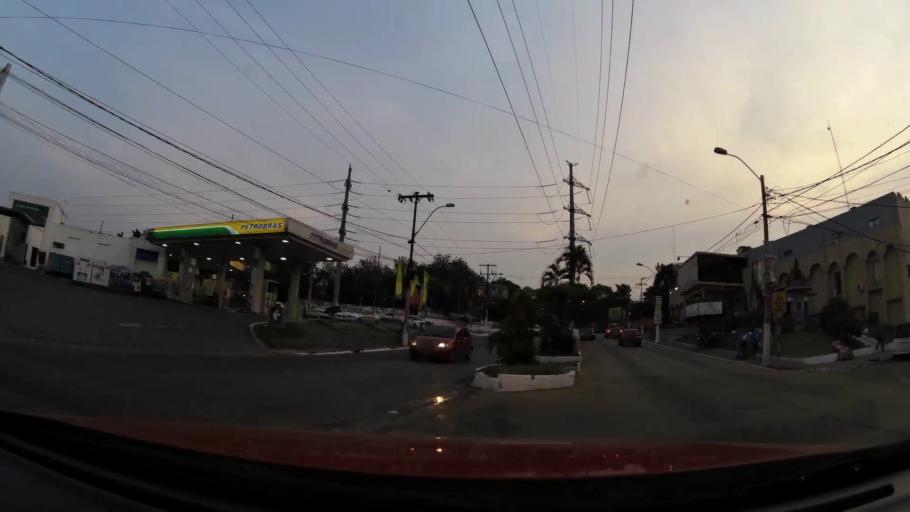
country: PY
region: Central
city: Lambare
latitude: -25.3418
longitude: -57.6250
